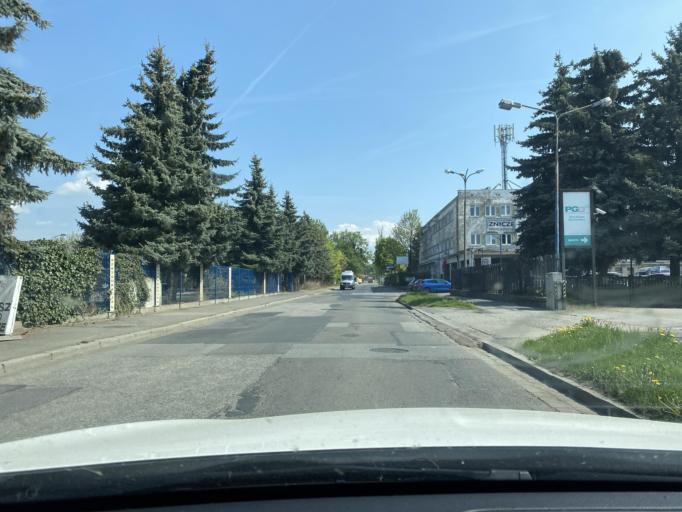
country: PL
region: Lower Silesian Voivodeship
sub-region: Powiat trzebnicki
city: Psary
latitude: 51.1504
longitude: 17.0230
